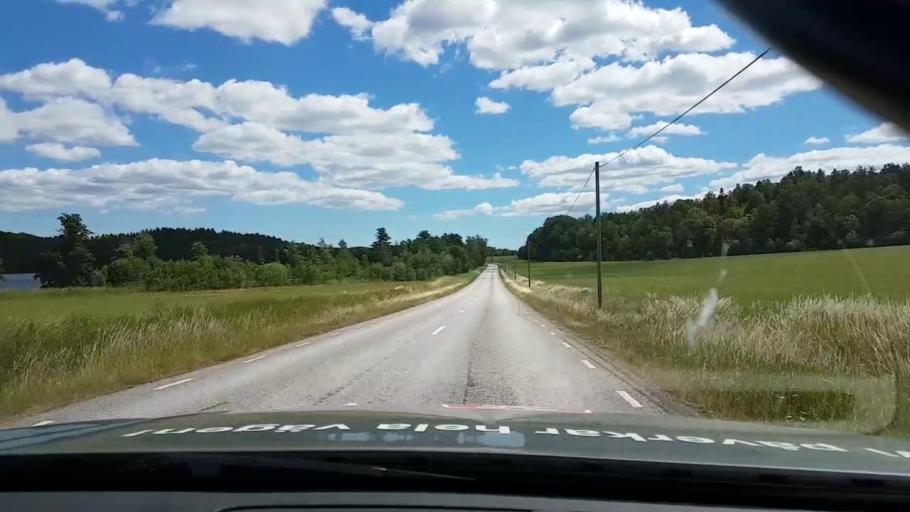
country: SE
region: Kalmar
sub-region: Vasterviks Kommun
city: Forserum
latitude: 58.0448
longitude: 16.4171
